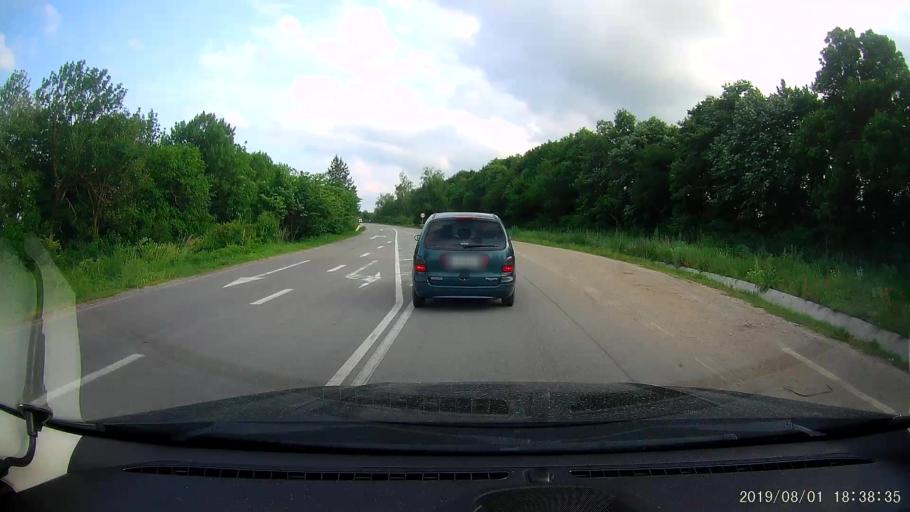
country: BG
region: Shumen
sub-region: Obshtina Khitrino
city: Gara Khitrino
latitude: 43.4000
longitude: 26.9158
